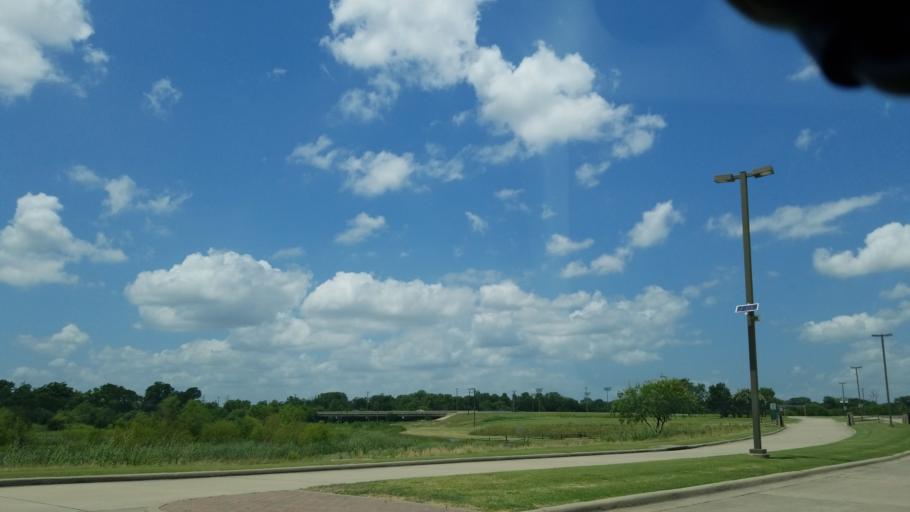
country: US
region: Texas
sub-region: Dallas County
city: Carrollton
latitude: 32.9632
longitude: -96.9403
